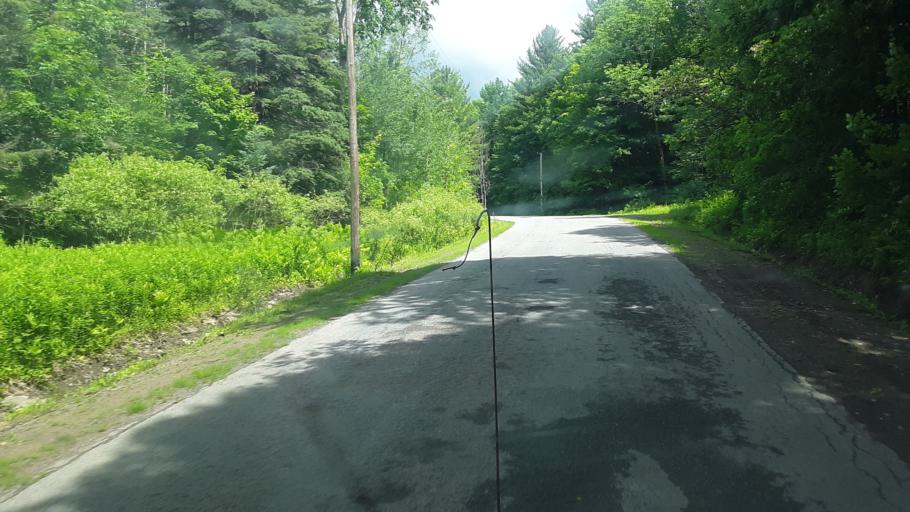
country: US
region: New York
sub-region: Oneida County
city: Rome
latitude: 43.3933
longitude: -75.5167
